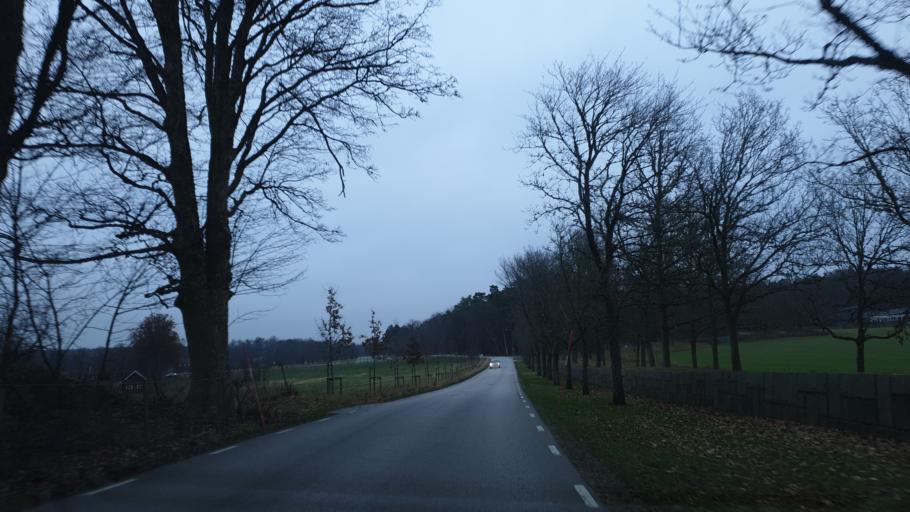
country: SE
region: Blekinge
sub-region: Karlskrona Kommun
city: Rodeby
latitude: 56.2138
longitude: 15.6779
